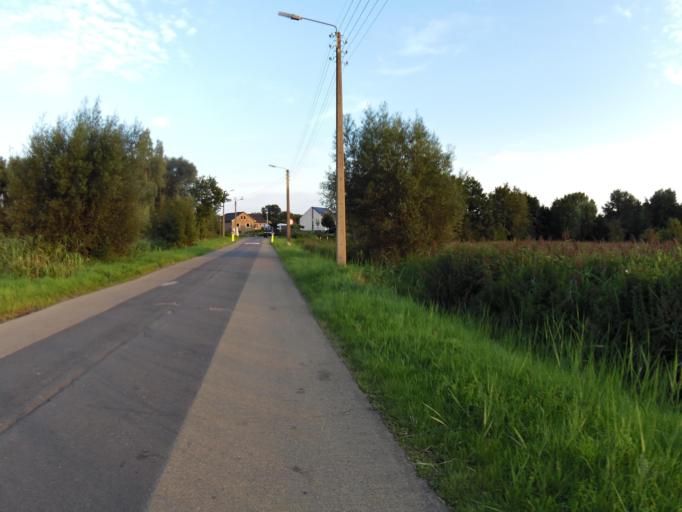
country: BE
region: Flanders
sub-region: Provincie Limburg
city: Tongeren
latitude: 50.7723
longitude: 5.5199
